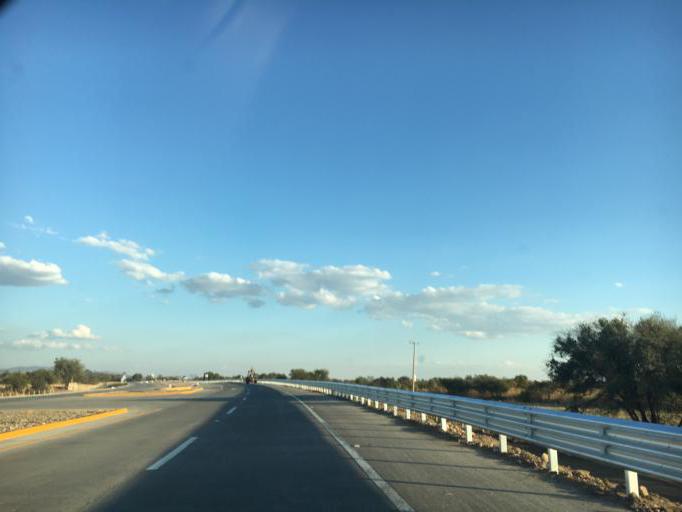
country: MX
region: Guanajuato
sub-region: Leon
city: Fraccionamiento Paraiso Real
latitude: 21.0994
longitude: -101.5729
